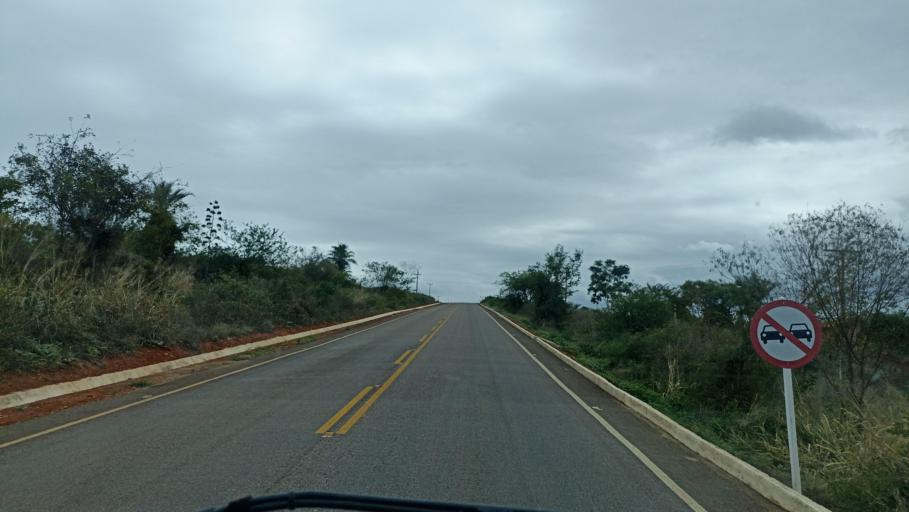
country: BR
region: Bahia
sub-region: Andarai
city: Vera Cruz
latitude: -12.9973
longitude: -40.9947
